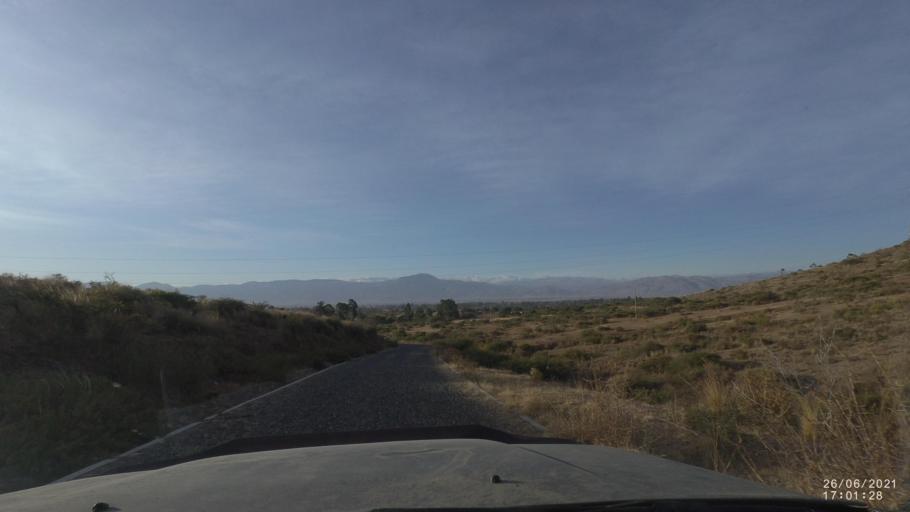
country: BO
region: Cochabamba
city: Cliza
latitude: -17.6609
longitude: -65.9109
